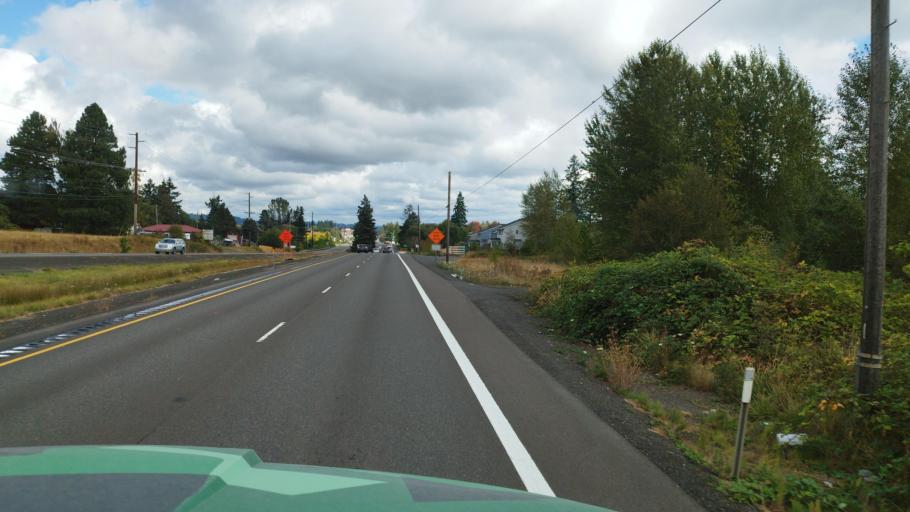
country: US
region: Oregon
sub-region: Washington County
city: Sherwood
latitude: 45.3570
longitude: -122.8622
